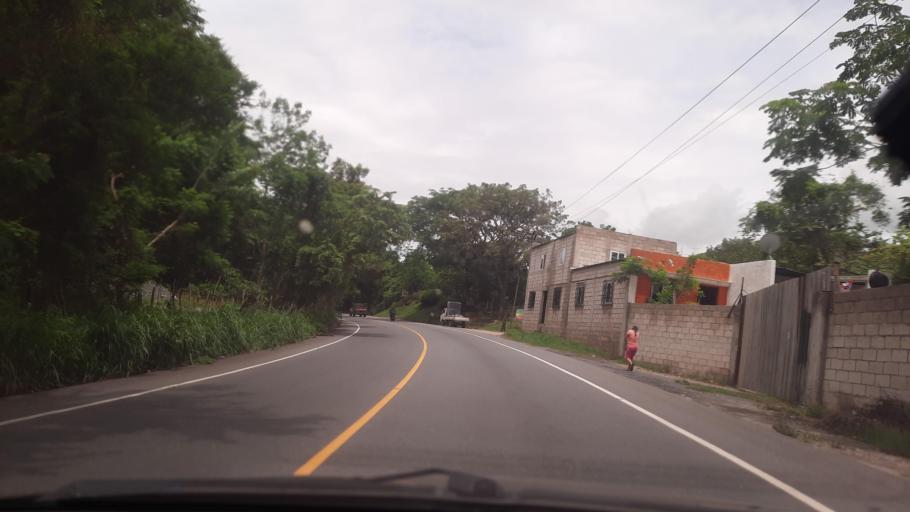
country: GT
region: Izabal
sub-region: Municipio de Los Amates
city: Los Amates
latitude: 15.2158
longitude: -89.2357
